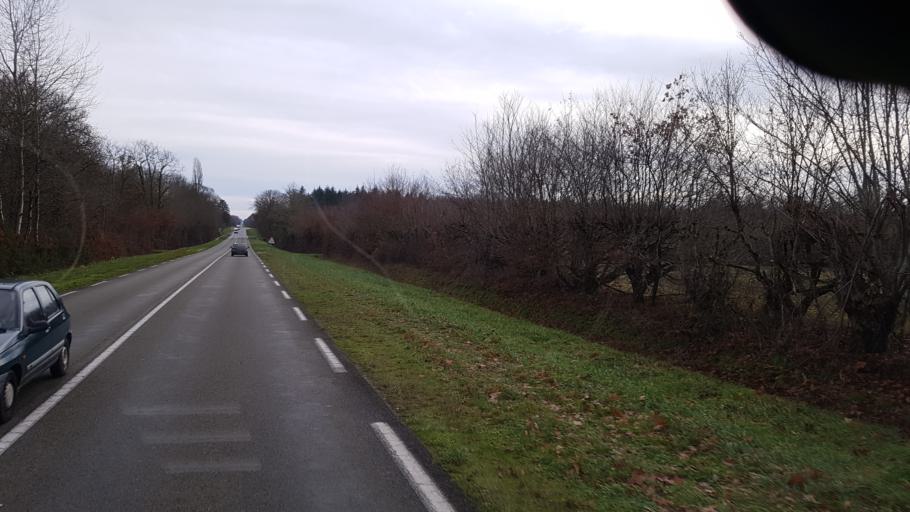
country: FR
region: Centre
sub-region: Departement du Loiret
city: La Ferte-Saint-Aubin
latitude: 47.6904
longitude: 1.9569
